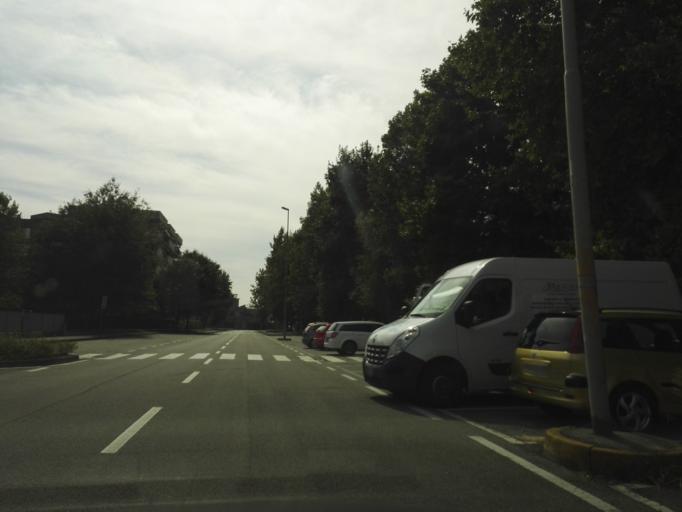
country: IT
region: Lombardy
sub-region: Citta metropolitana di Milano
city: Bettola-Zeloforomagno
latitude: 45.4275
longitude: 9.3027
